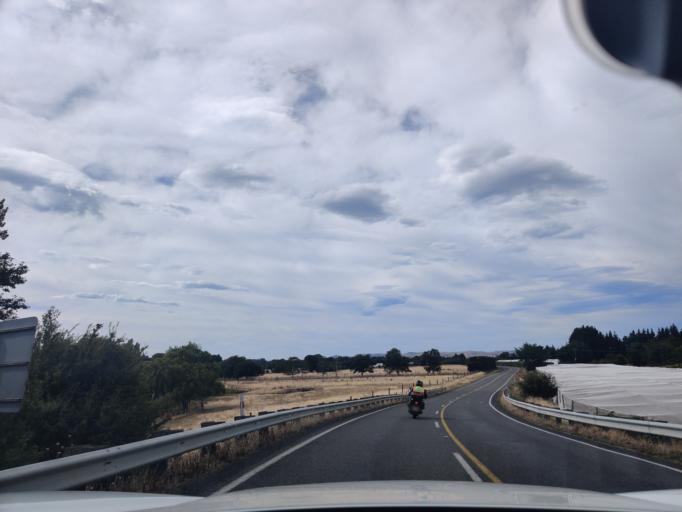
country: NZ
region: Wellington
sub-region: Masterton District
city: Masterton
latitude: -40.8955
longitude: 175.6626
